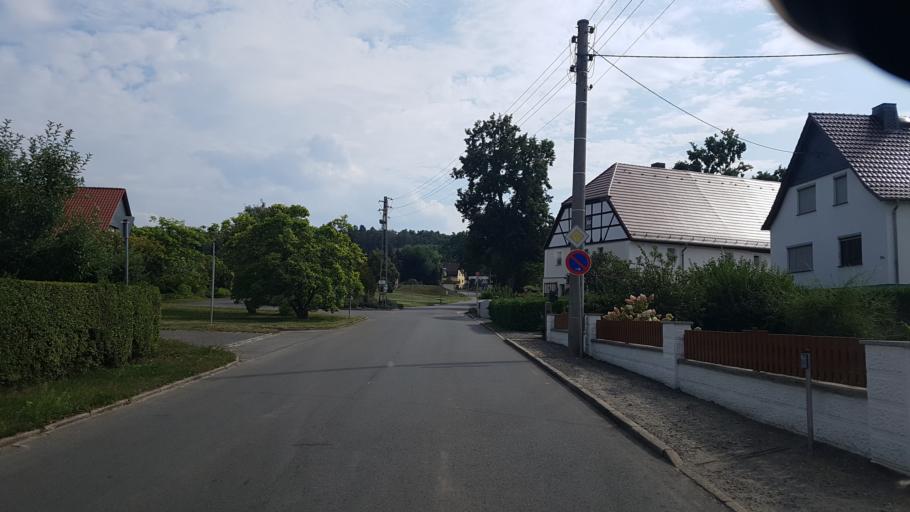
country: DE
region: Brandenburg
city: Grosskmehlen
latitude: 51.3754
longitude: 13.7236
